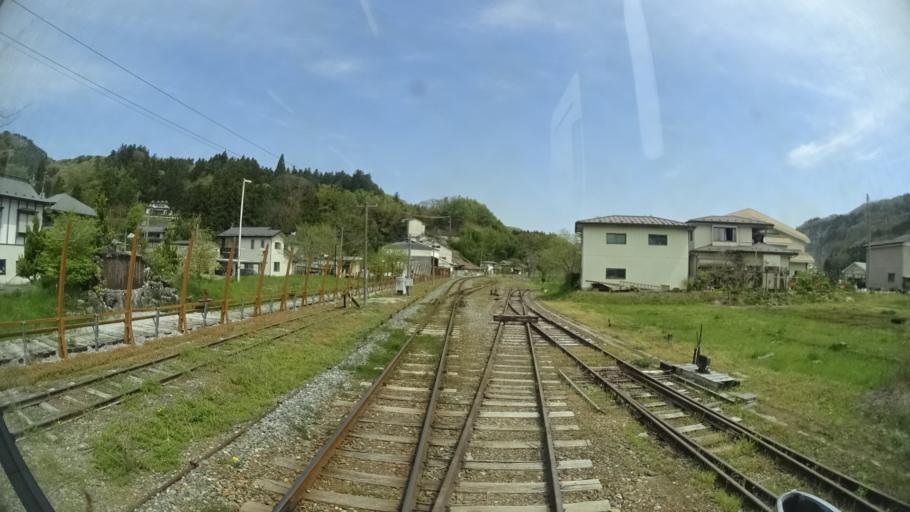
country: JP
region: Iwate
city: Ichinoseki
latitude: 38.9790
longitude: 141.2389
